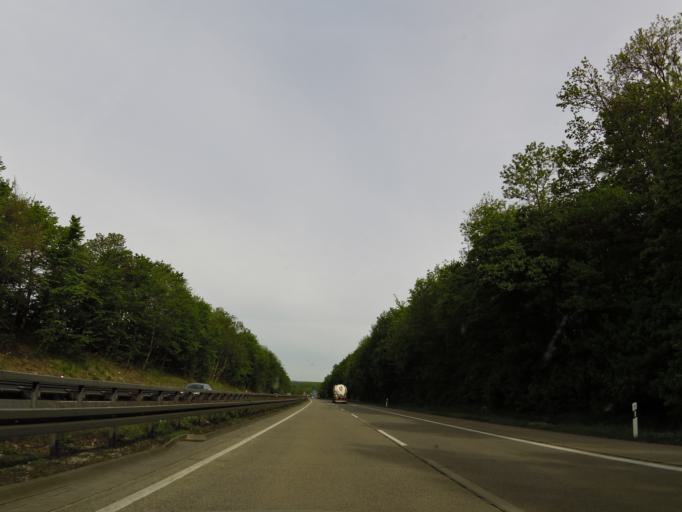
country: DE
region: Lower Saxony
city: Holle
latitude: 52.0946
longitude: 10.1667
